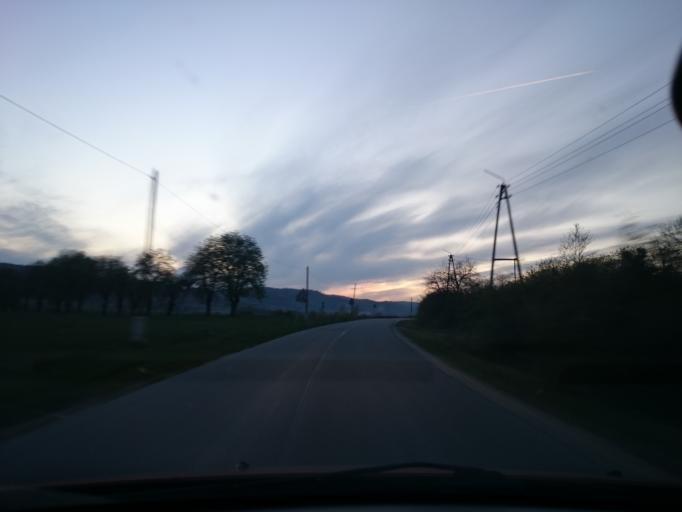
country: PL
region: Lower Silesian Voivodeship
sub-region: Powiat zabkowicki
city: Budzow
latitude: 50.5547
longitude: 16.7071
